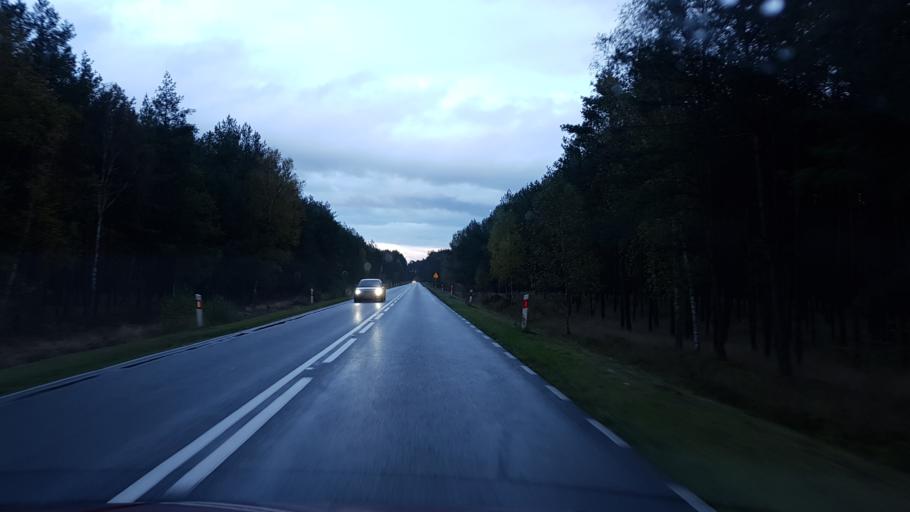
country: PL
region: Greater Poland Voivodeship
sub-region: Powiat pilski
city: Pila
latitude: 53.1897
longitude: 16.8155
